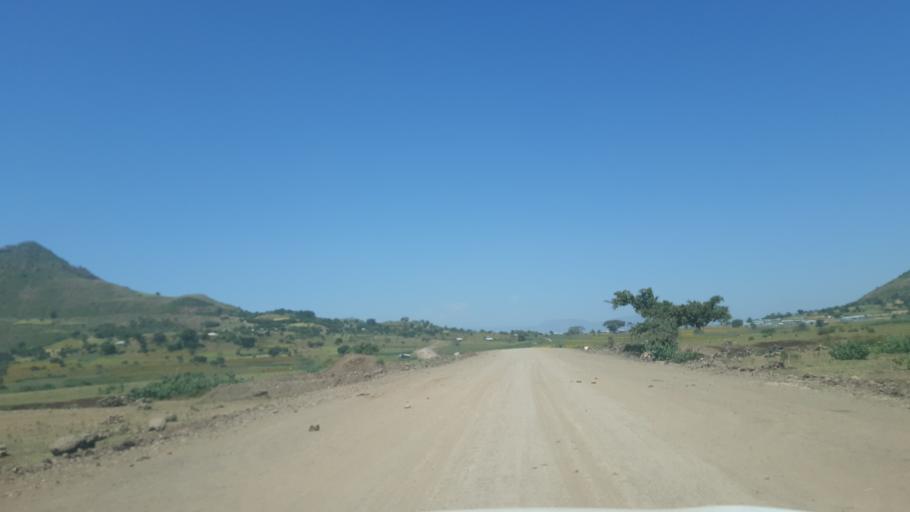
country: ET
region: Amhara
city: Dabat
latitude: 13.1554
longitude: 37.6138
